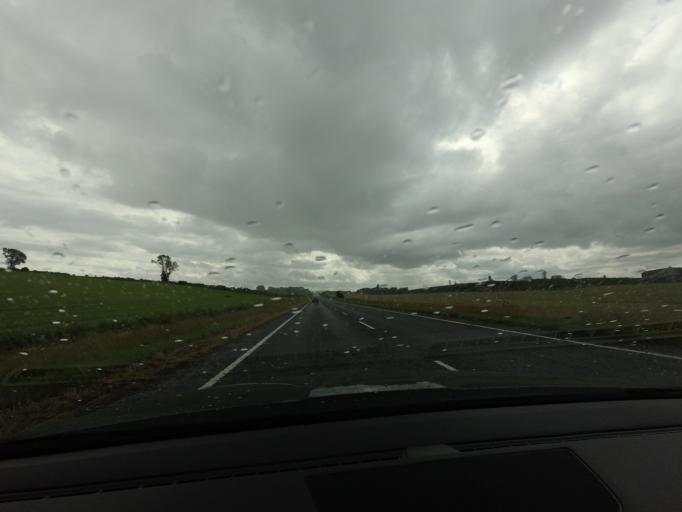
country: GB
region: Scotland
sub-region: Highland
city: Fortrose
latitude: 57.5193
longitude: -4.0734
